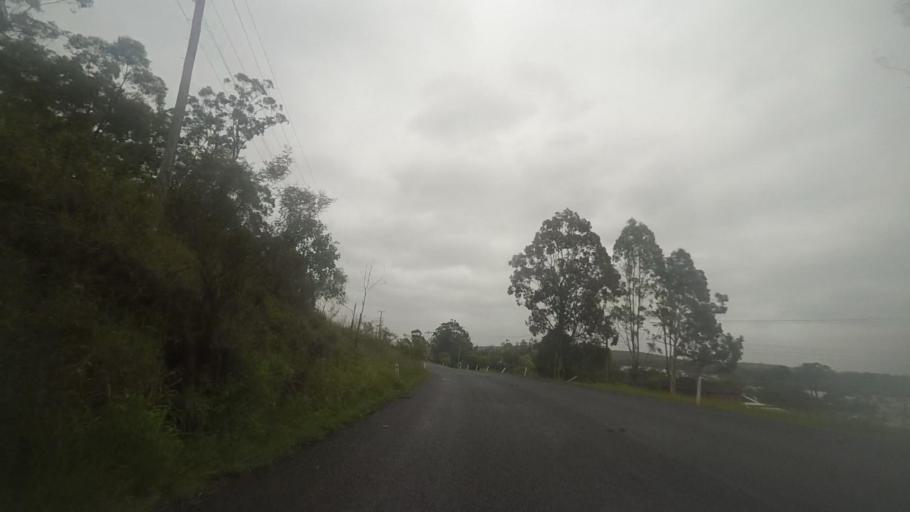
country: AU
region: New South Wales
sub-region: Port Stephens Shire
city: Port Stephens
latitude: -32.6503
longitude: 151.9731
